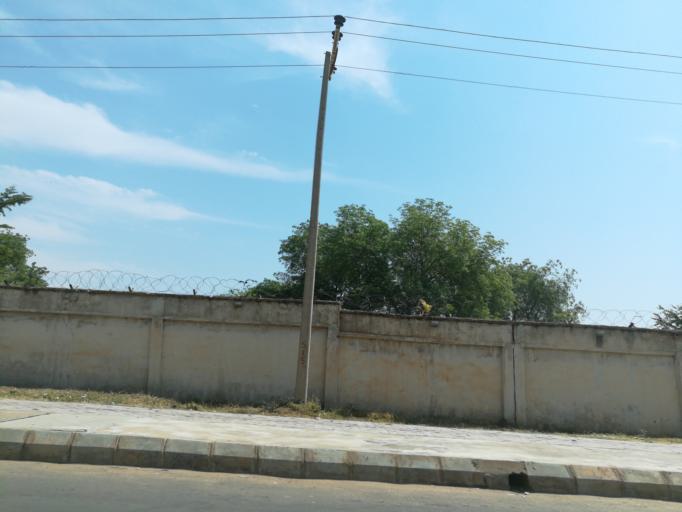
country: NG
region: Kano
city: Kano
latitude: 12.0327
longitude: 8.5241
